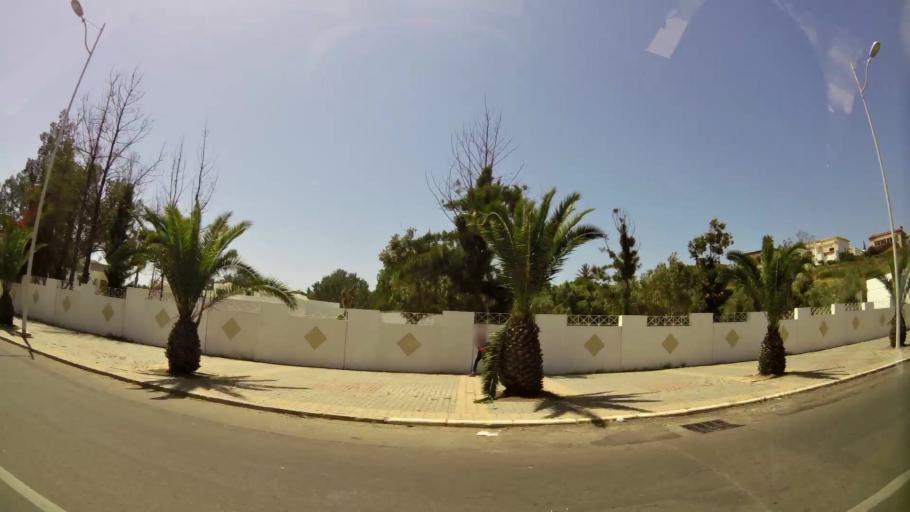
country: MA
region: Souss-Massa-Draa
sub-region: Agadir-Ida-ou-Tnan
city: Agadir
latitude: 30.4283
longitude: -9.5926
